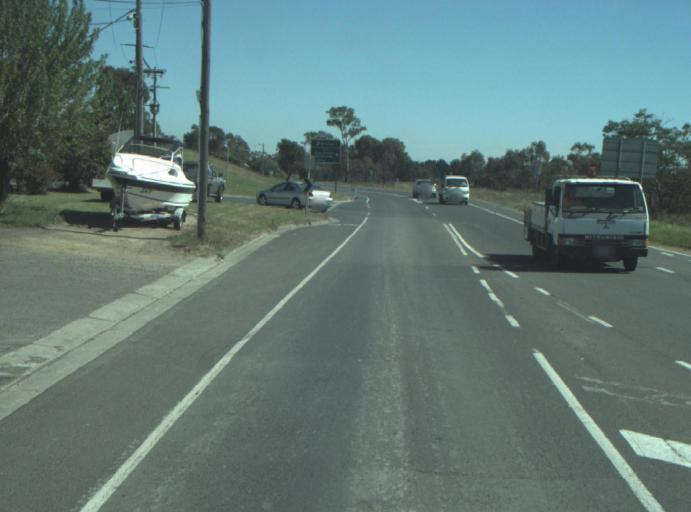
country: AU
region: Victoria
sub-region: Greater Geelong
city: Breakwater
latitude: -38.1783
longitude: 144.3537
